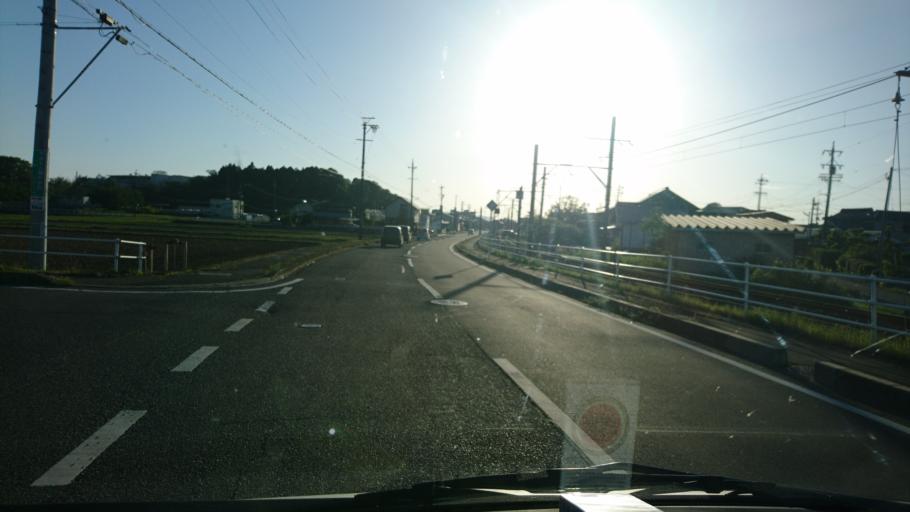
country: JP
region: Gifu
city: Mitake
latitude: 35.4258
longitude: 137.0719
